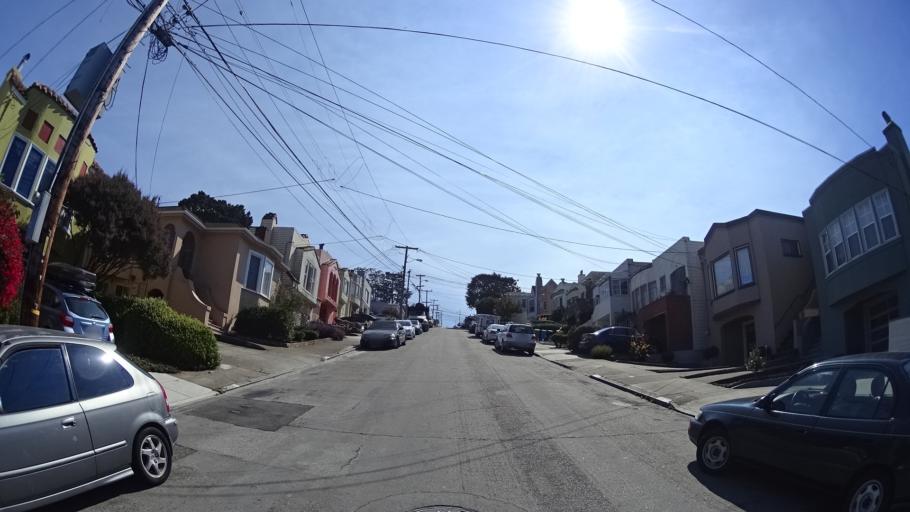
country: US
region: California
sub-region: San Mateo County
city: Daly City
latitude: 37.7206
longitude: -122.4634
